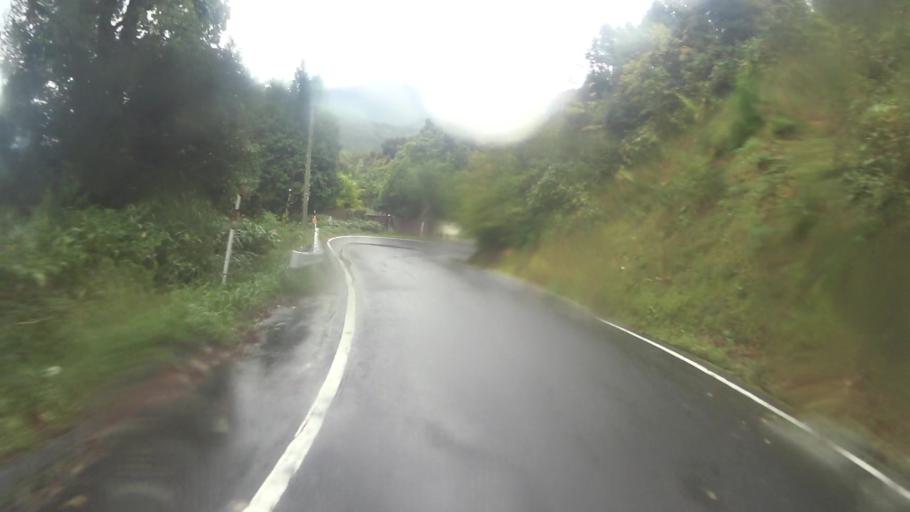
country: JP
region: Kyoto
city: Miyazu
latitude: 35.4841
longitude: 135.1593
